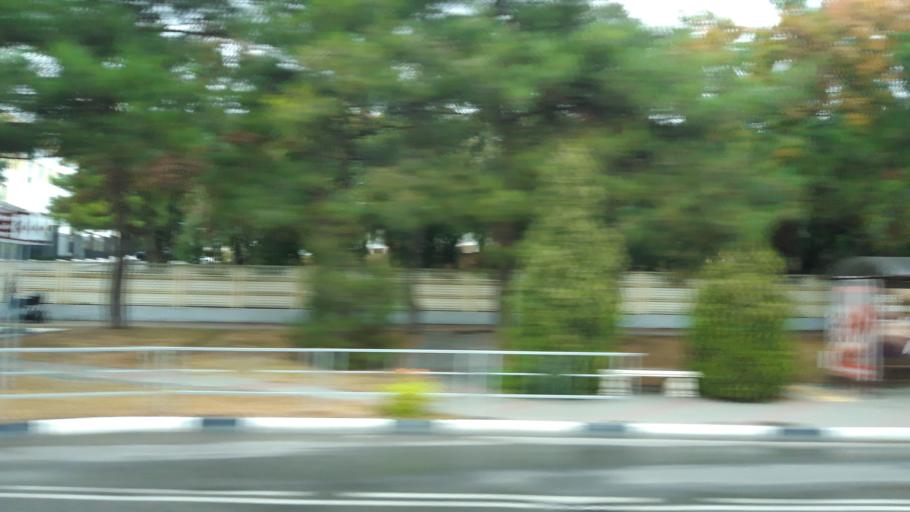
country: RU
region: Krasnodarskiy
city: Gelendzhik
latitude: 44.5806
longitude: 38.0658
